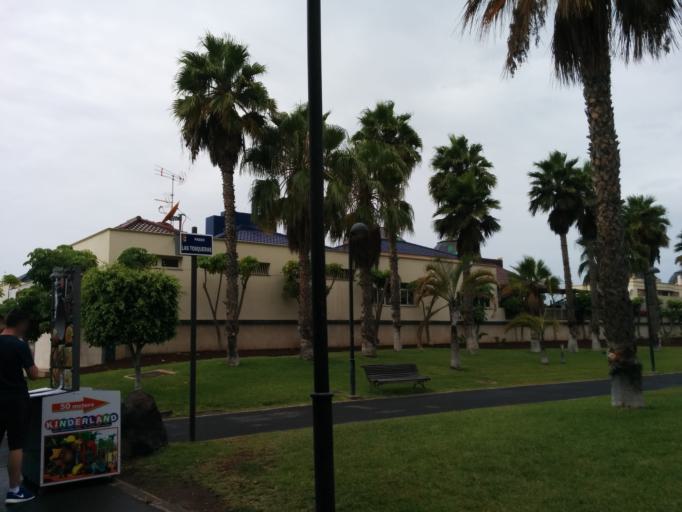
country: ES
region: Canary Islands
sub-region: Provincia de Santa Cruz de Tenerife
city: Playa de las Americas
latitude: 28.0558
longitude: -16.7301
